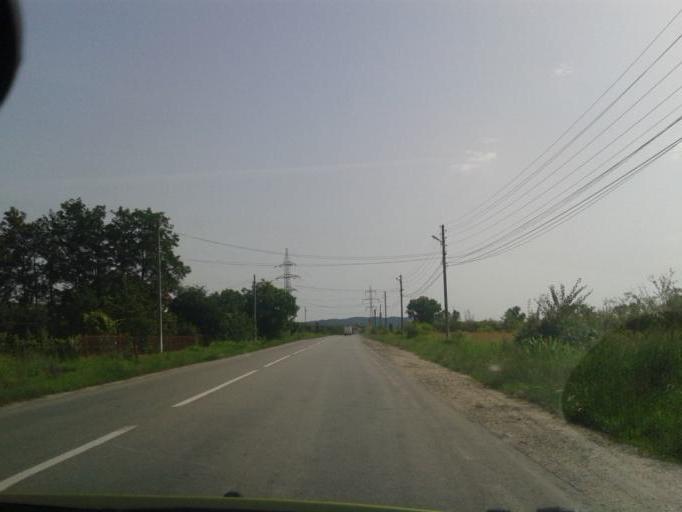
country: RO
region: Valcea
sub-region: Comuna Mihaesti
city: Mihaesti
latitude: 45.0487
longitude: 24.2748
